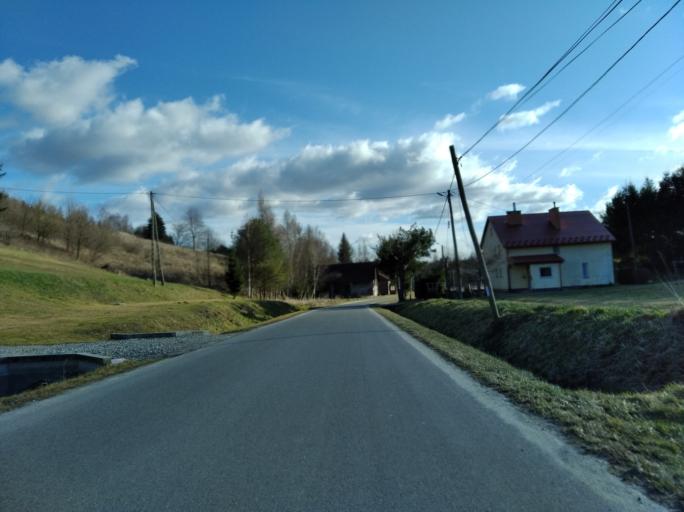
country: PL
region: Subcarpathian Voivodeship
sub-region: Powiat strzyzowski
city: Wisniowa
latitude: 49.8899
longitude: 21.7139
